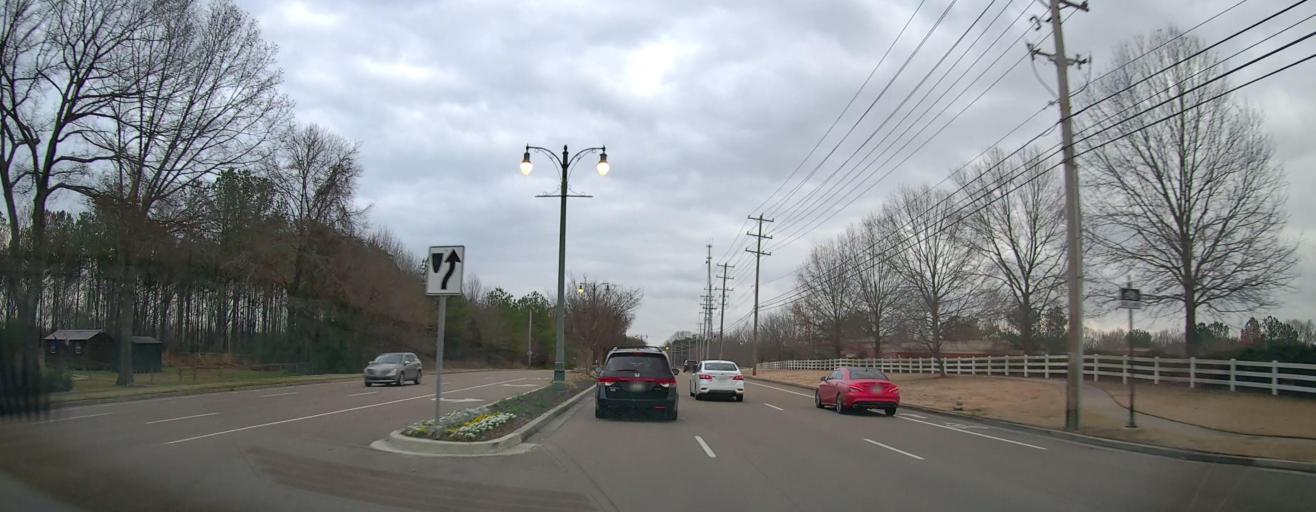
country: US
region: Tennessee
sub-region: Shelby County
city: Germantown
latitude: 35.0474
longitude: -89.7476
